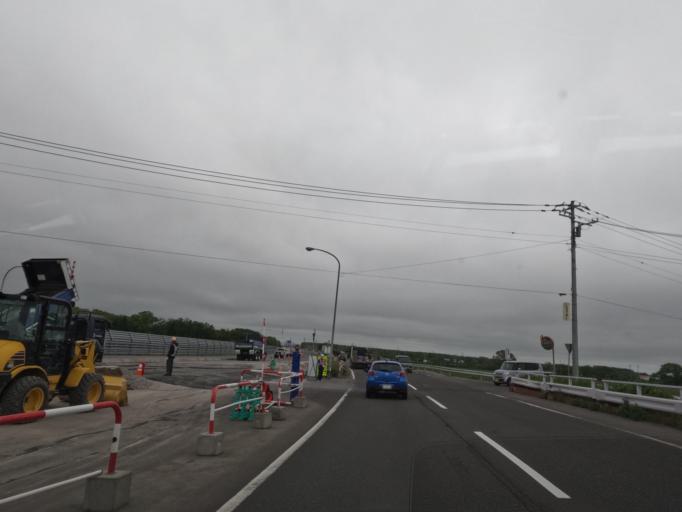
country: JP
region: Hokkaido
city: Ebetsu
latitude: 43.1409
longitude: 141.5161
